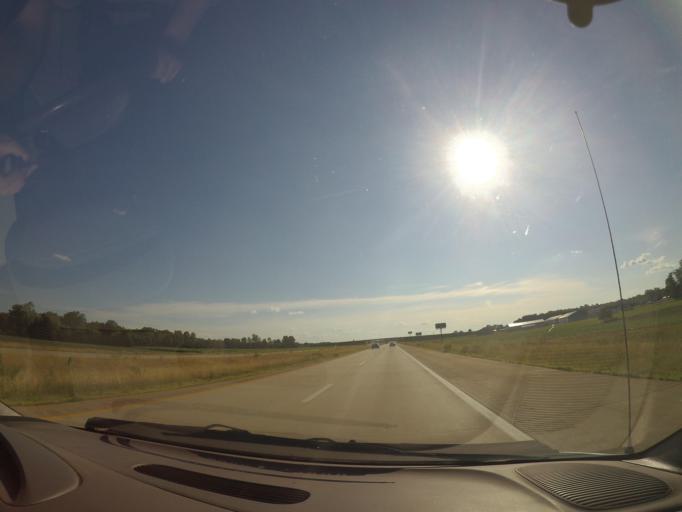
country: US
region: Ohio
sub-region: Lucas County
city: Whitehouse
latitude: 41.4359
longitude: -83.8665
